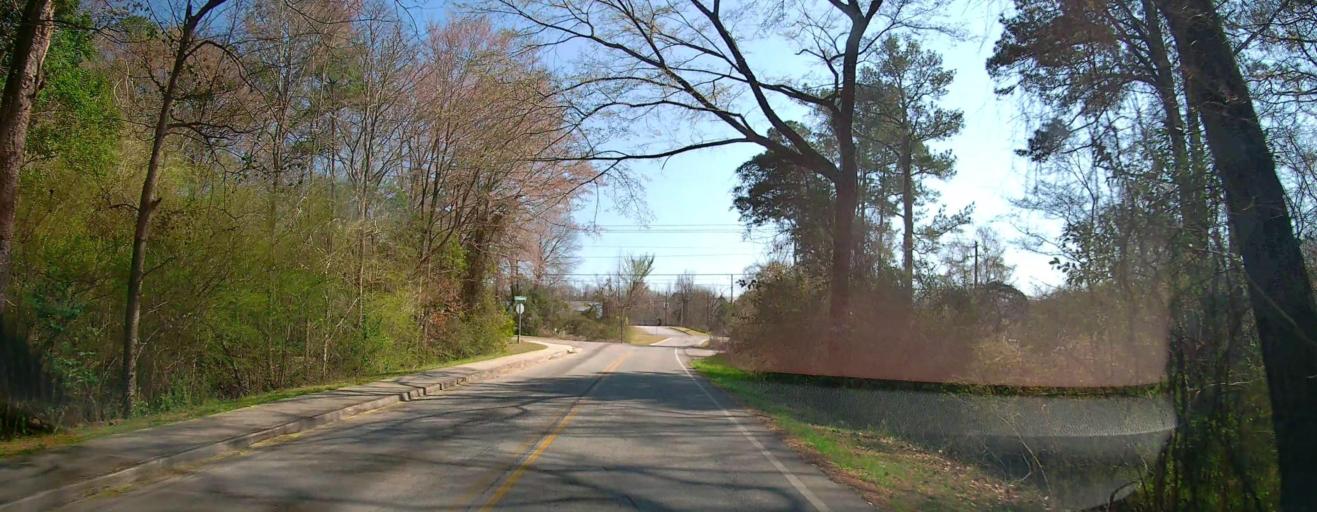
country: US
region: Georgia
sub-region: Bibb County
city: Macon
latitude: 32.8809
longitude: -83.6090
